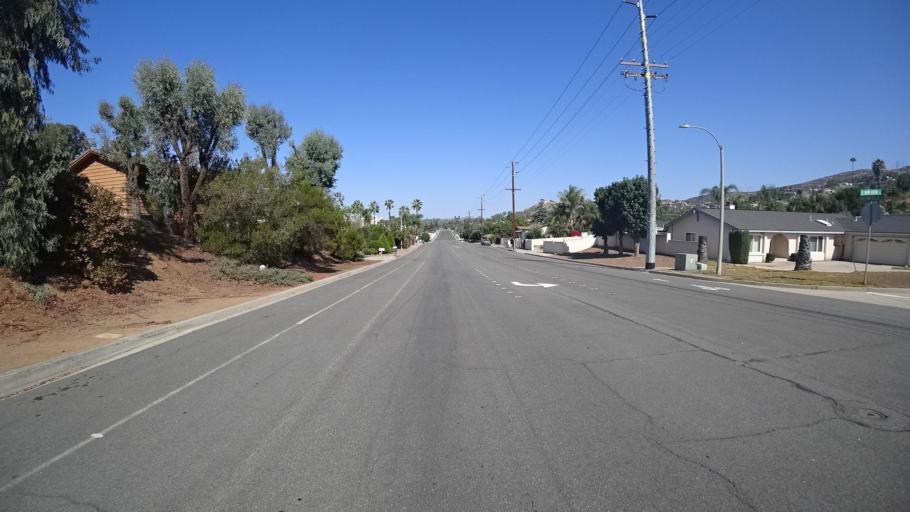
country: US
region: California
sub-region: San Diego County
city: Granite Hills
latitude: 32.7952
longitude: -116.9017
